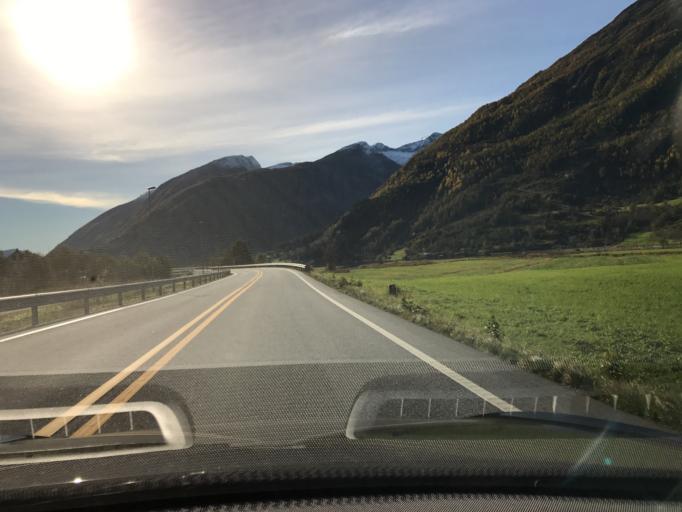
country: NO
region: Sogn og Fjordane
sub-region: Leikanger
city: Hermansverk
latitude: 61.4208
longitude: 6.7638
